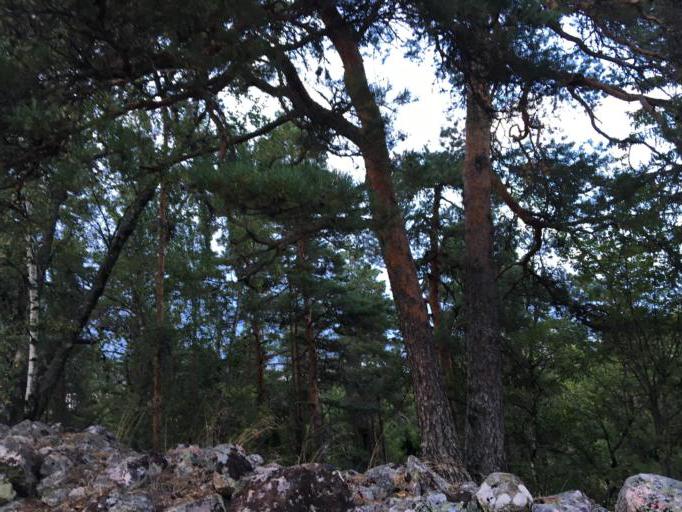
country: SE
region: Soedermanland
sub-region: Eskilstuna Kommun
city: Kvicksund
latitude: 59.4171
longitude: 16.3223
